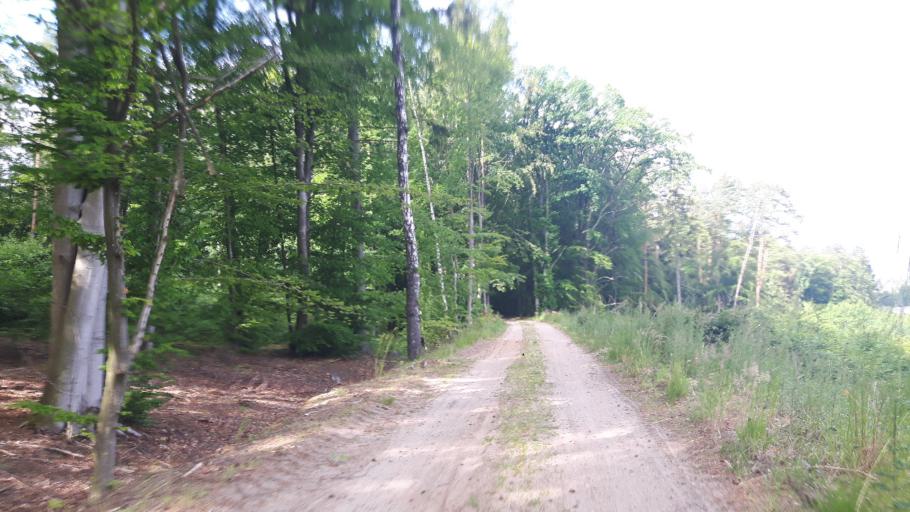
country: PL
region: Pomeranian Voivodeship
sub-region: Slupsk
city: Slupsk
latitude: 54.6020
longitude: 17.0188
